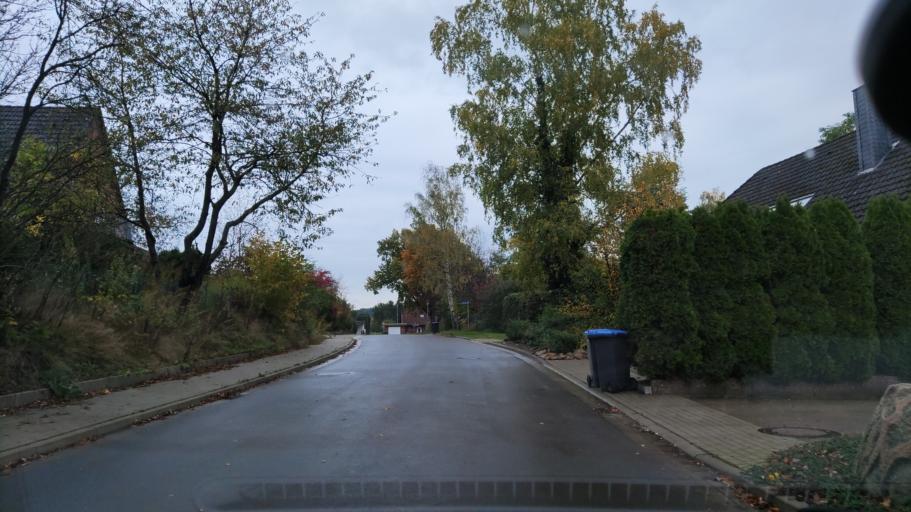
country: DE
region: Lower Saxony
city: Deutsch Evern
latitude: 53.1977
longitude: 10.4399
